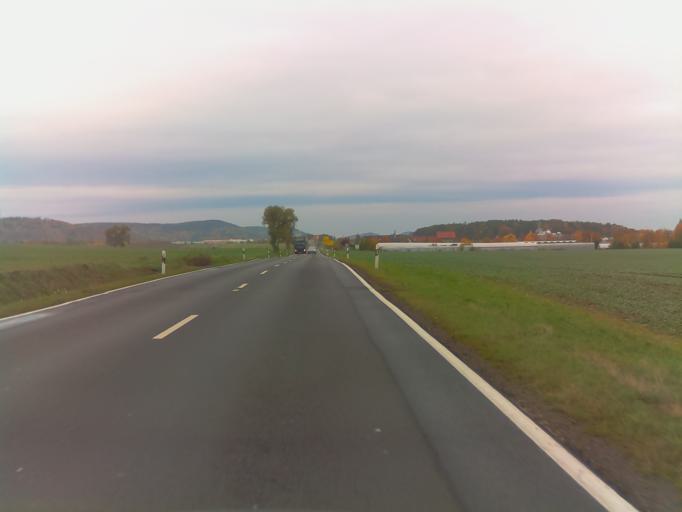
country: DE
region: Thuringia
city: Dornheim
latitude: 50.8257
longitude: 10.9942
